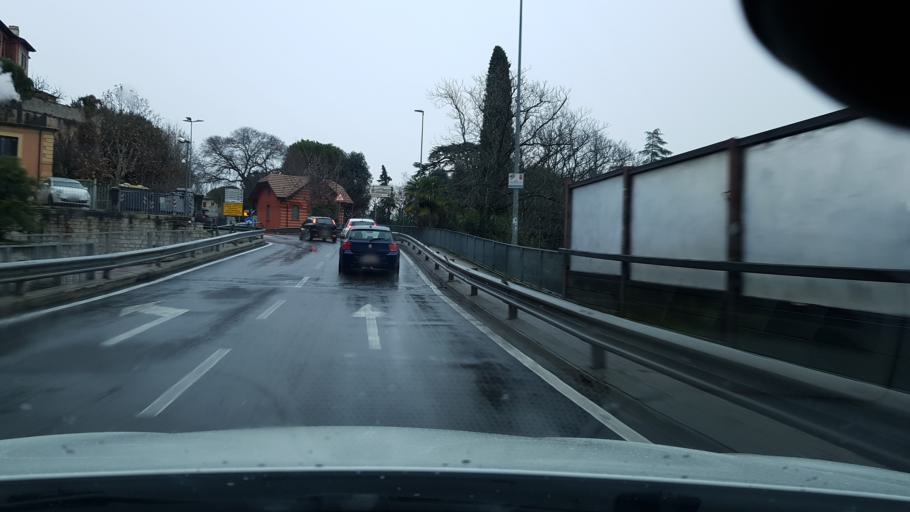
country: IT
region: Umbria
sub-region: Provincia di Perugia
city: Perugia
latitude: 43.1102
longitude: 12.3918
